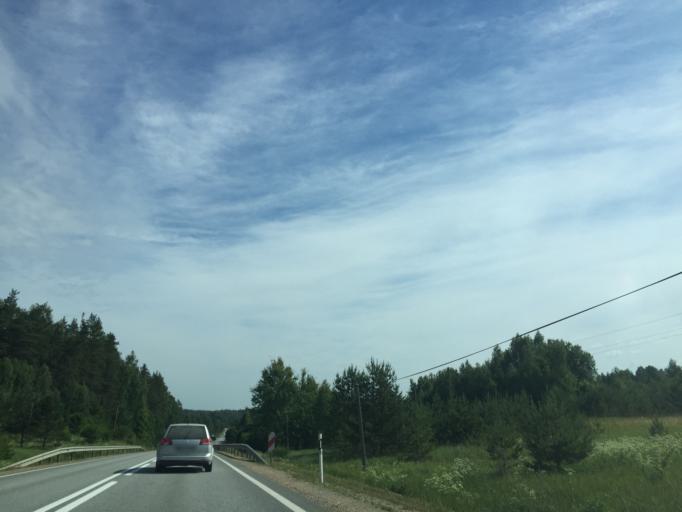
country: LV
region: Ligatne
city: Ligatne
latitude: 57.2877
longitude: 24.9152
